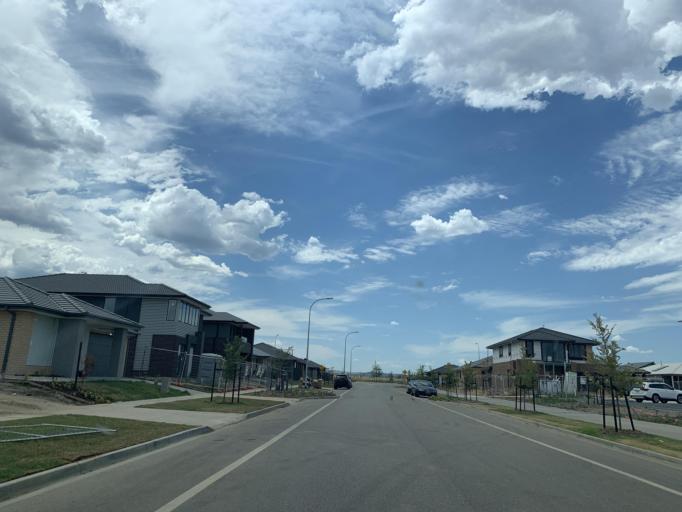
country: AU
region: Victoria
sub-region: Cardinia
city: Officer South
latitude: -38.1223
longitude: 145.3708
